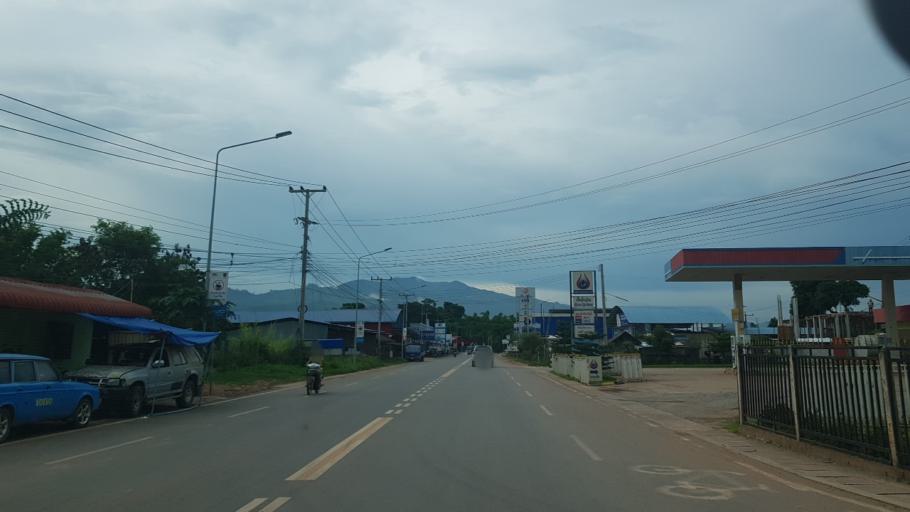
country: LA
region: Oudomxai
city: Muang Xay
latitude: 20.6687
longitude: 101.9825
